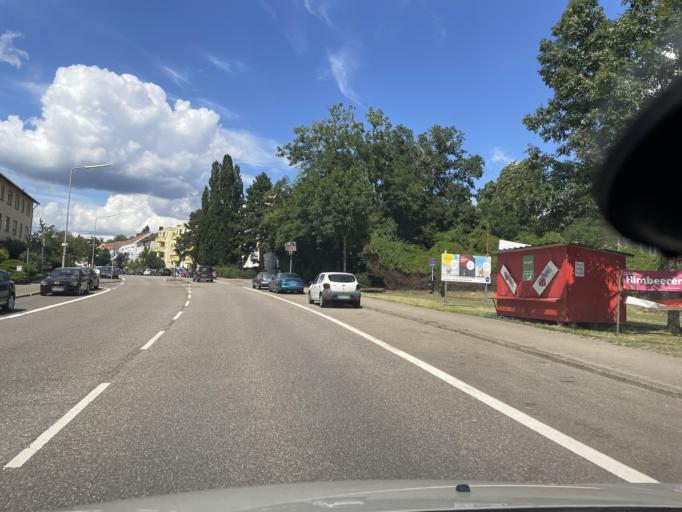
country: DE
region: Saarland
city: Saarbrucken
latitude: 49.2340
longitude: 7.0211
